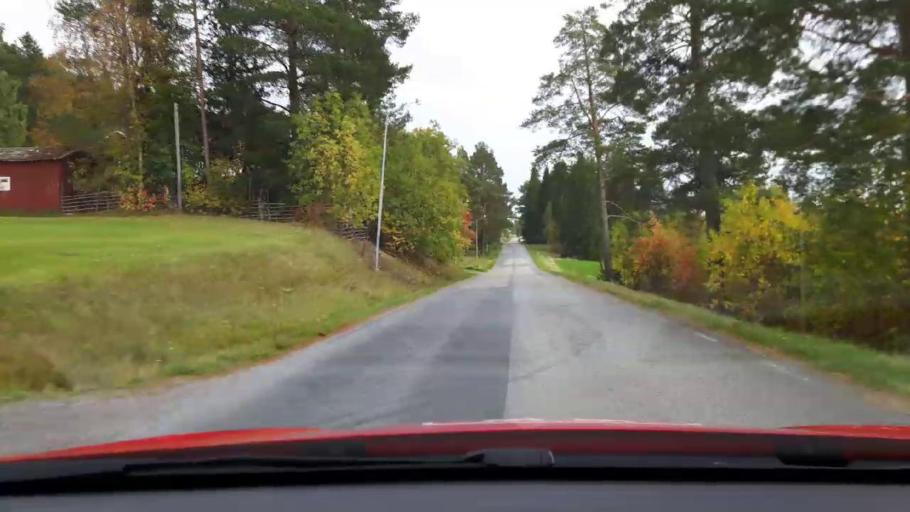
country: SE
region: Jaemtland
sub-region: Krokoms Kommun
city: Valla
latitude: 63.2565
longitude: 14.0205
